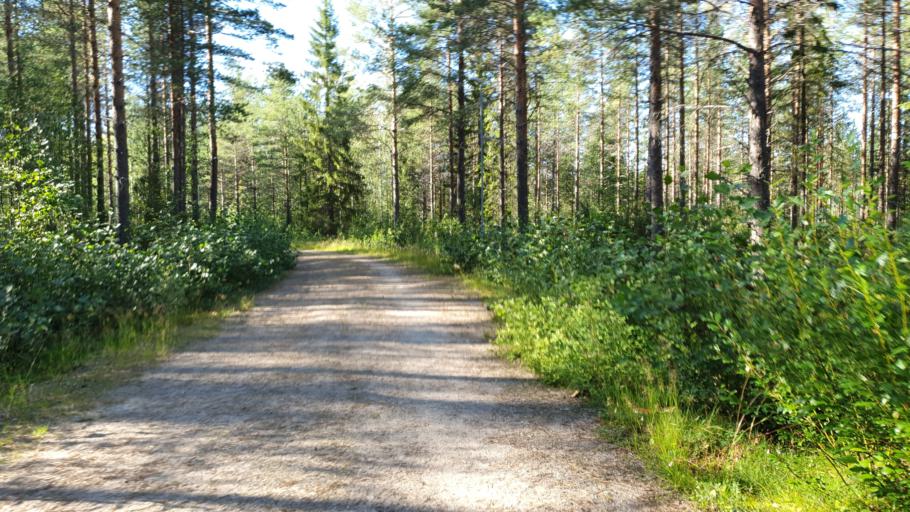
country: FI
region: Kainuu
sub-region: Kehys-Kainuu
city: Kuhmo
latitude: 64.1134
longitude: 29.5028
